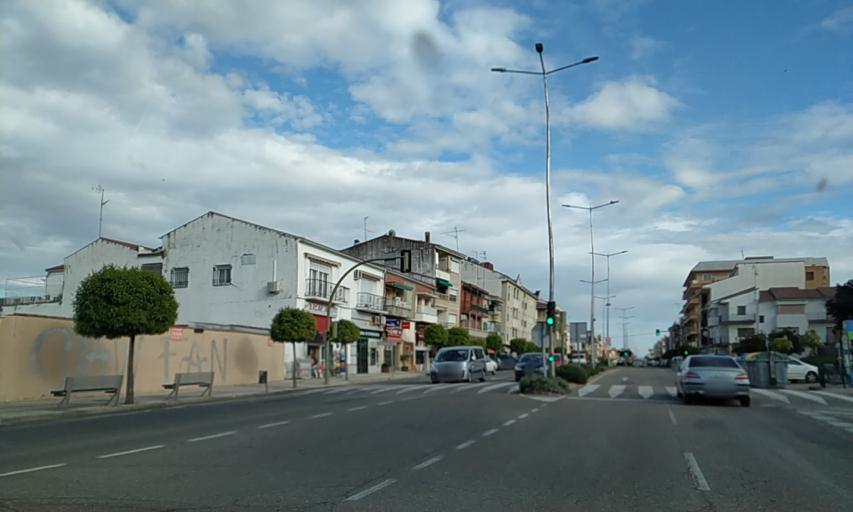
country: ES
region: Extremadura
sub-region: Provincia de Caceres
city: Moraleja
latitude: 40.0702
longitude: -6.6575
